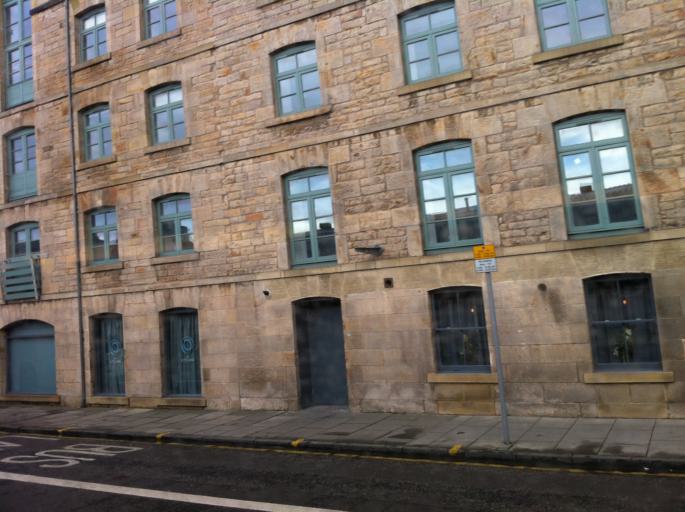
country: GB
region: Scotland
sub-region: West Lothian
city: Seafield
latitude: 55.9764
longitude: -3.1702
